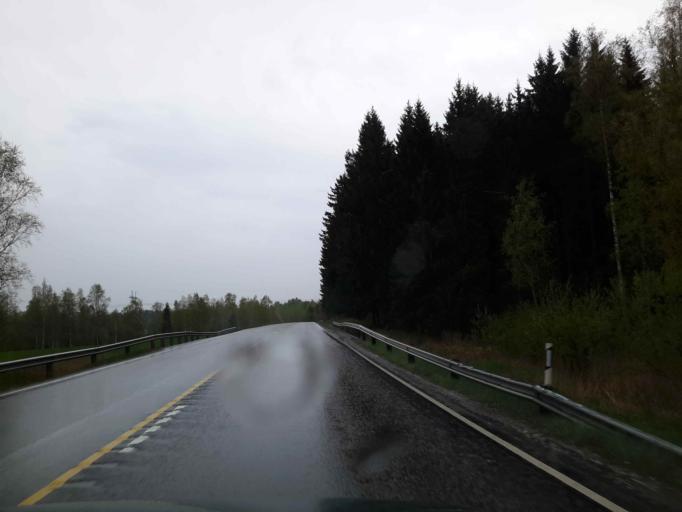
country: FI
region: Uusimaa
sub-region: Helsinki
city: Vihti
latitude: 60.3855
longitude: 24.5125
